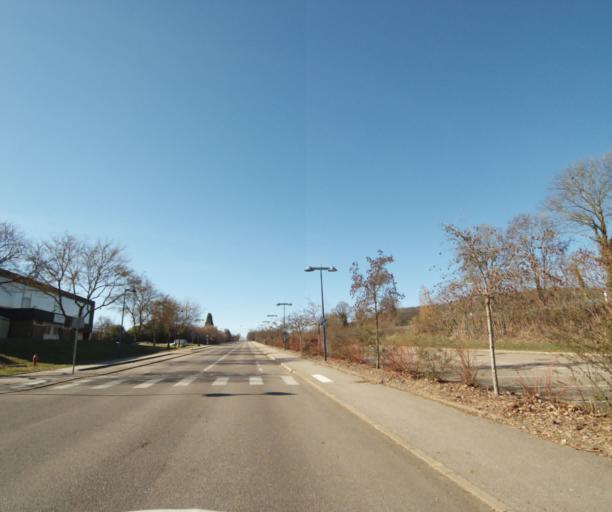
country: FR
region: Lorraine
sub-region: Departement de Meurthe-et-Moselle
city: Ludres
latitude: 48.6199
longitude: 6.1668
